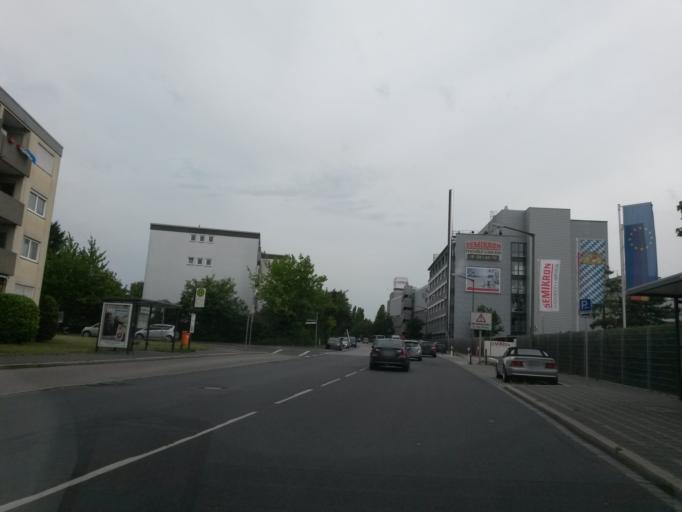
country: DE
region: Bavaria
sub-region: Regierungsbezirk Mittelfranken
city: Grossreuth bei Schweinau
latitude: 49.4427
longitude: 11.0053
